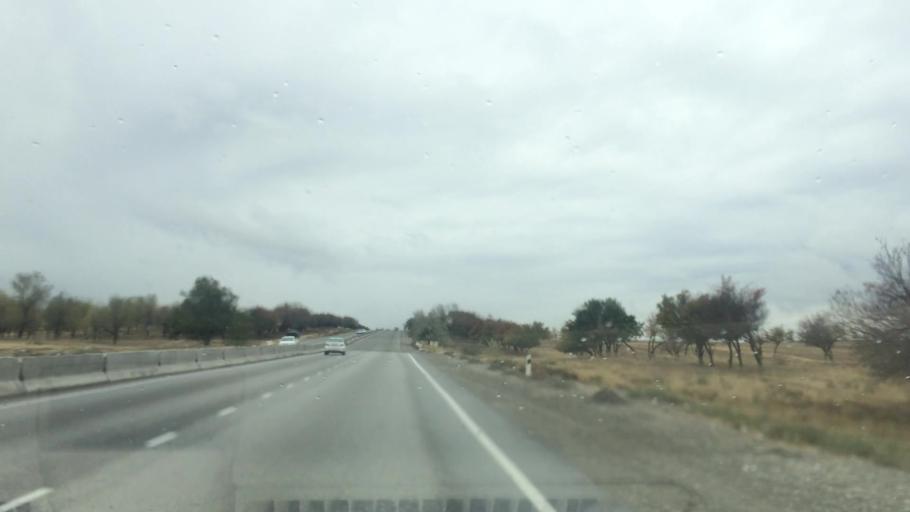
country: UZ
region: Samarqand
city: Bulung'ur
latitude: 39.8630
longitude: 67.4719
